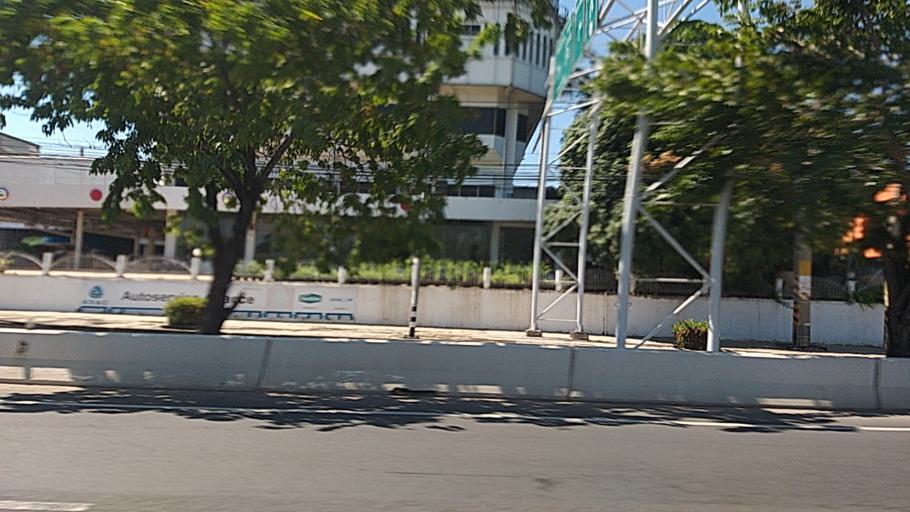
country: TH
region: Nakhon Ratchasima
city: Nakhon Ratchasima
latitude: 14.9660
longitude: 102.0644
